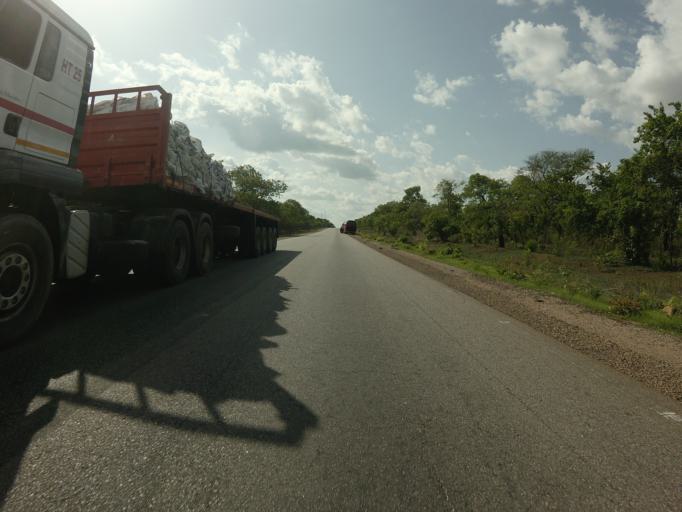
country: GH
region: Upper East
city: Bolgatanga
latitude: 10.5406
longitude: -0.8236
